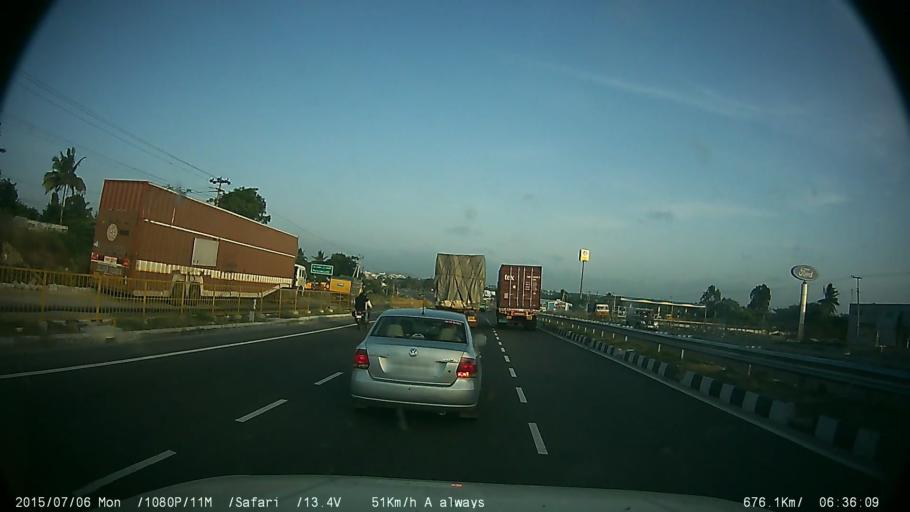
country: IN
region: Tamil Nadu
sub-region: Krishnagiri
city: Hosur
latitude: 12.7106
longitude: 77.8971
